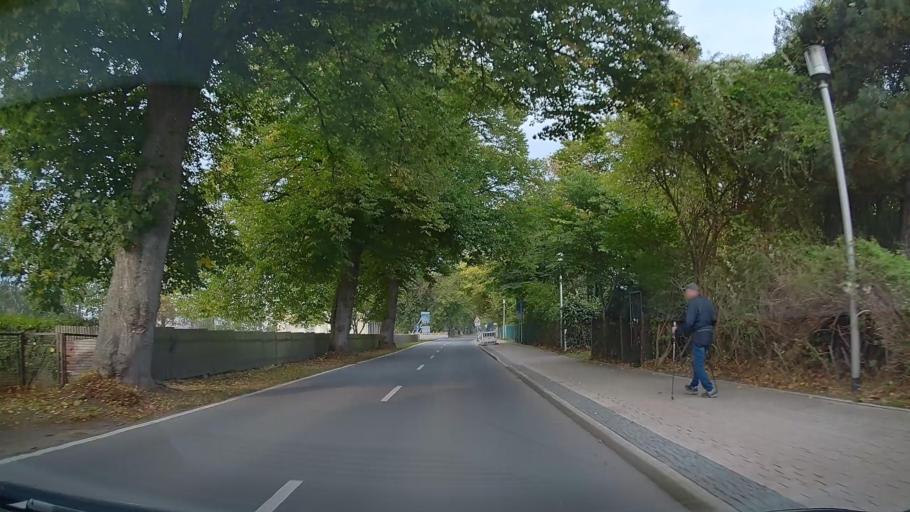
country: DE
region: Mecklenburg-Vorpommern
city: Bad Doberan
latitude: 54.1373
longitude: 11.8371
